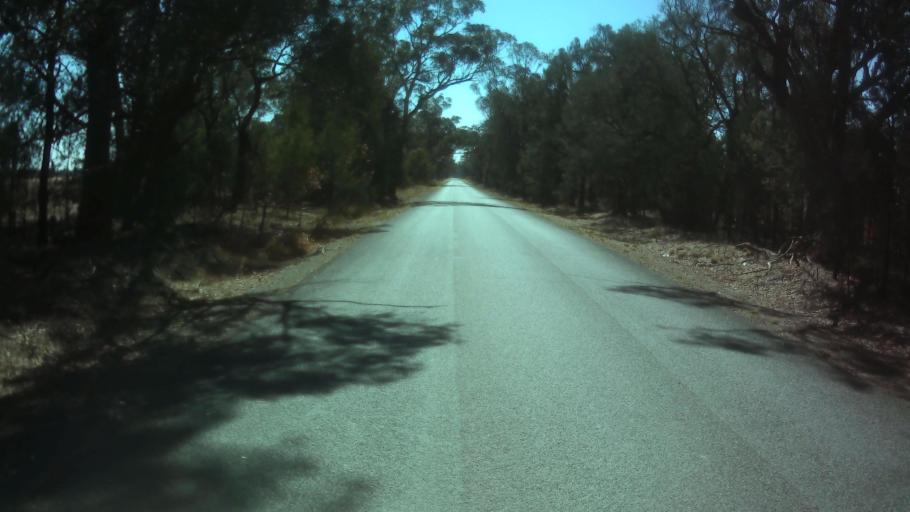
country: AU
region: New South Wales
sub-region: Weddin
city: Grenfell
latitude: -33.8138
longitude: 147.9274
